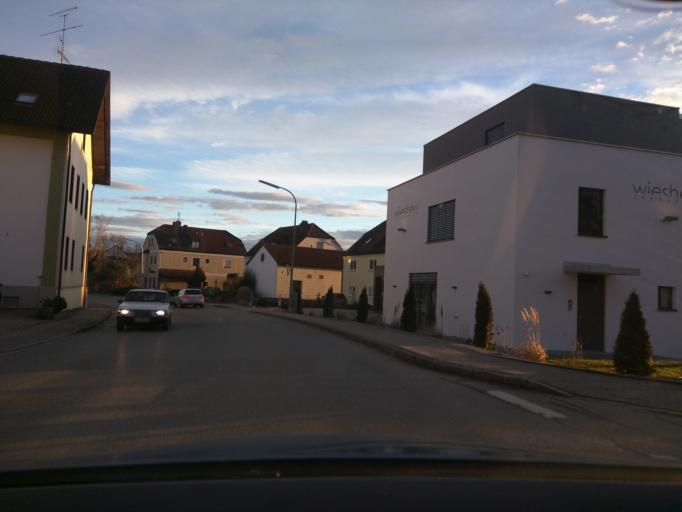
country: DE
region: Bavaria
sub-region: Upper Bavaria
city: Attenkirchen
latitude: 48.5051
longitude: 11.7581
